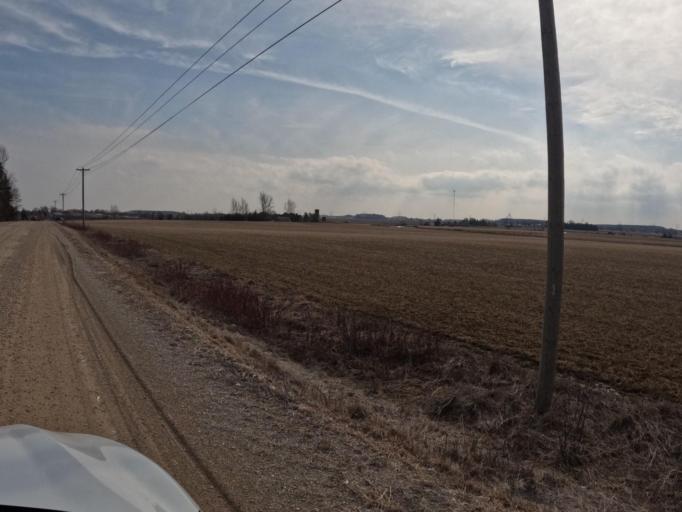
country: CA
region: Ontario
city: Orangeville
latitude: 43.8820
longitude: -80.2972
